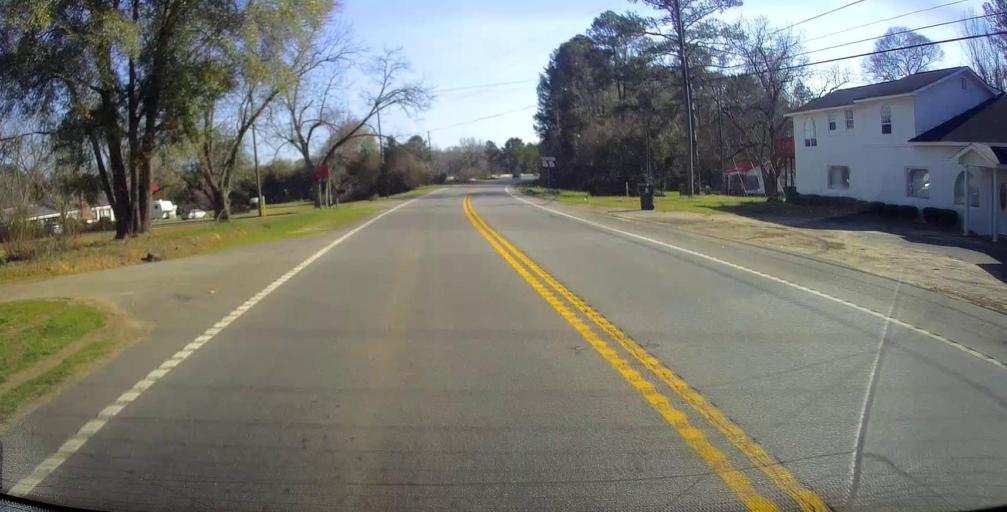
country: US
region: Georgia
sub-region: Macon County
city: Oglethorpe
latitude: 32.3162
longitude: -84.0653
